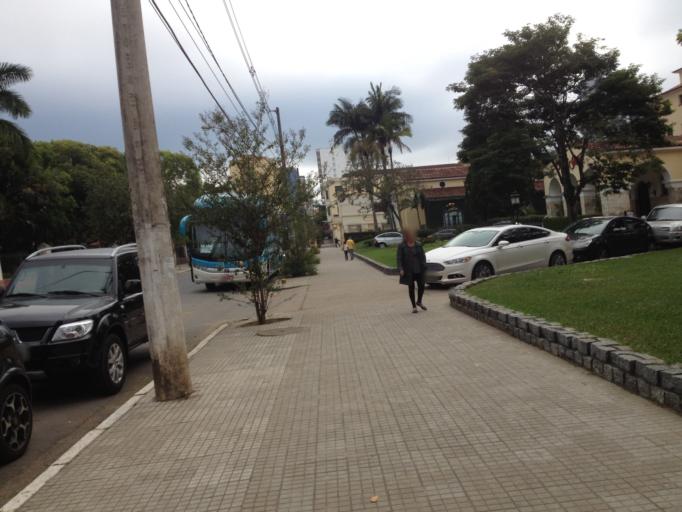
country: BR
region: Minas Gerais
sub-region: Caxambu
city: Caxambu
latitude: -21.9817
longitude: -44.9352
